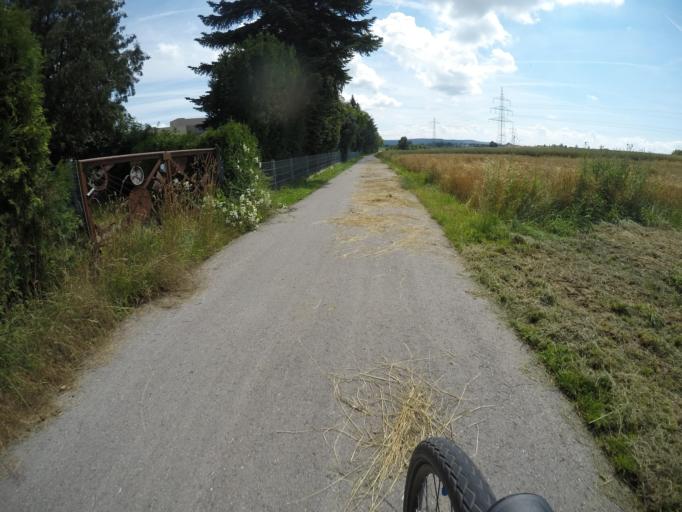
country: DE
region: Baden-Wuerttemberg
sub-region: Regierungsbezirk Stuttgart
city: Deckenpfronn
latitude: 48.6195
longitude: 8.8350
